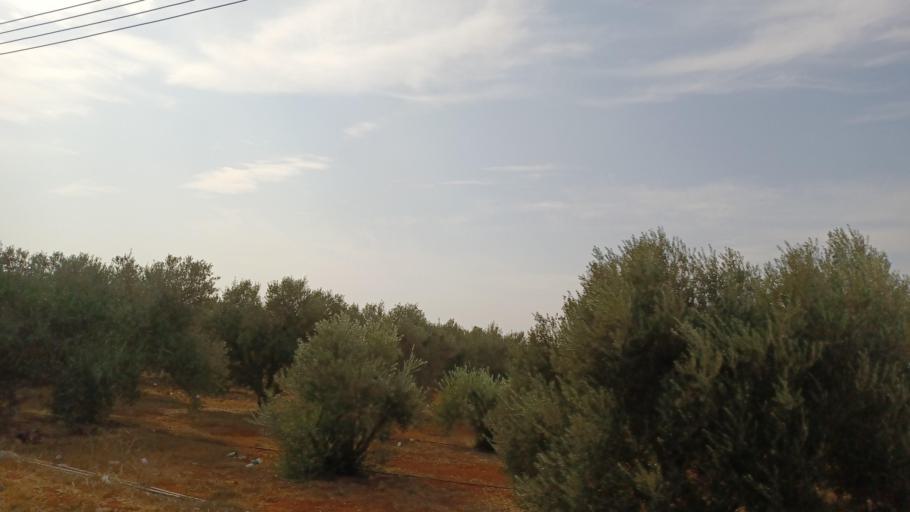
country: CY
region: Ammochostos
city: Liopetri
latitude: 34.9867
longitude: 33.8940
